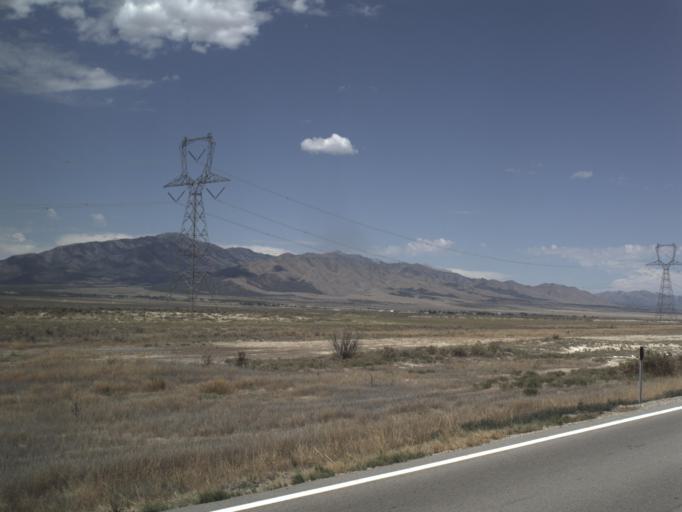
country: US
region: Utah
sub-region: Tooele County
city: Tooele
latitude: 40.2975
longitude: -112.4019
